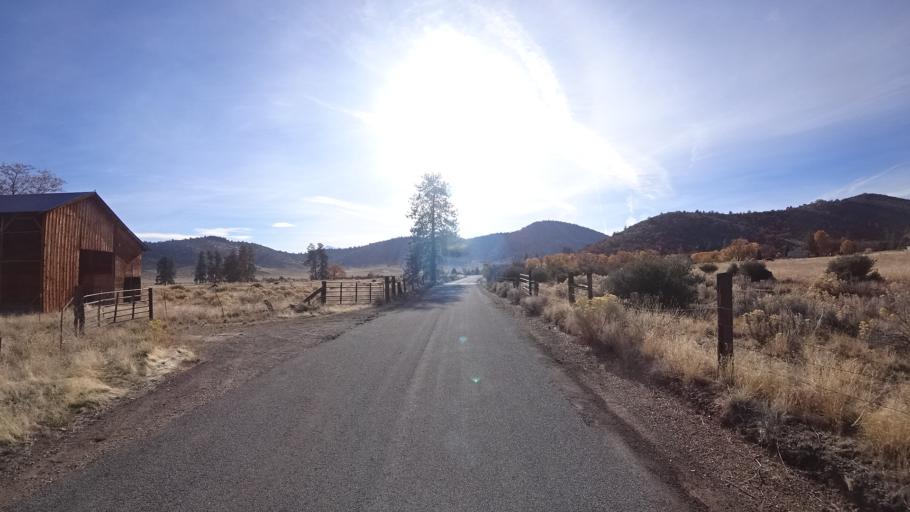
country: US
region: California
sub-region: Siskiyou County
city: Montague
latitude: 41.6381
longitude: -122.5728
